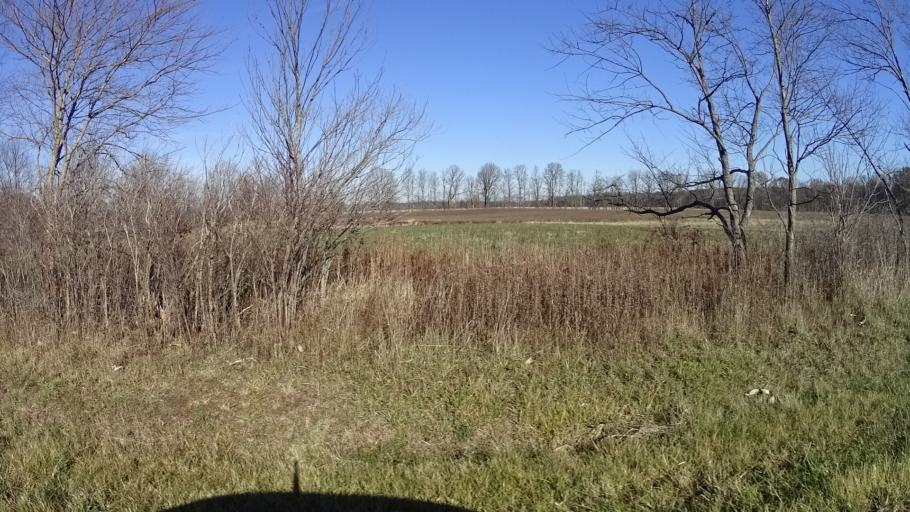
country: US
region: Ohio
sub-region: Huron County
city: New London
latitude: 41.1158
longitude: -82.3445
